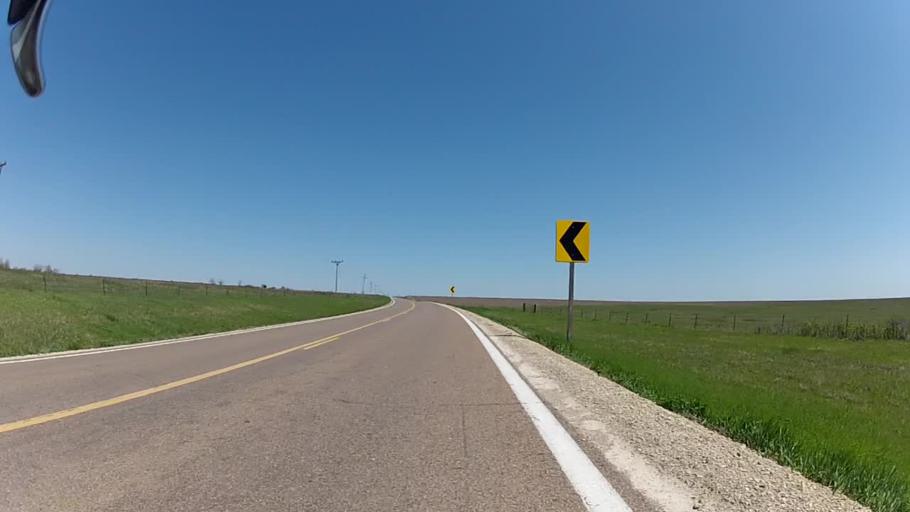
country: US
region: Kansas
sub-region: Wabaunsee County
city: Alma
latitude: 38.9326
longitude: -96.5203
